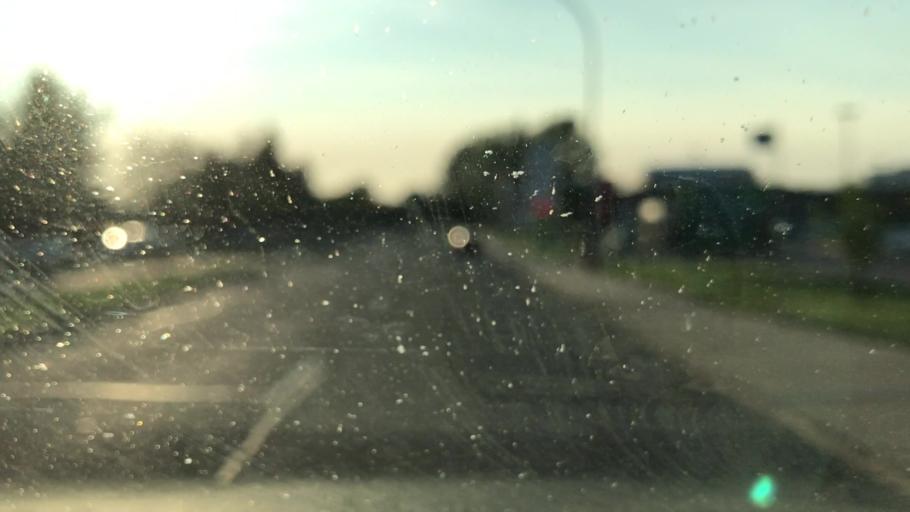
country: CA
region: Alberta
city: Edmonton
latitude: 53.5242
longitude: -113.4261
